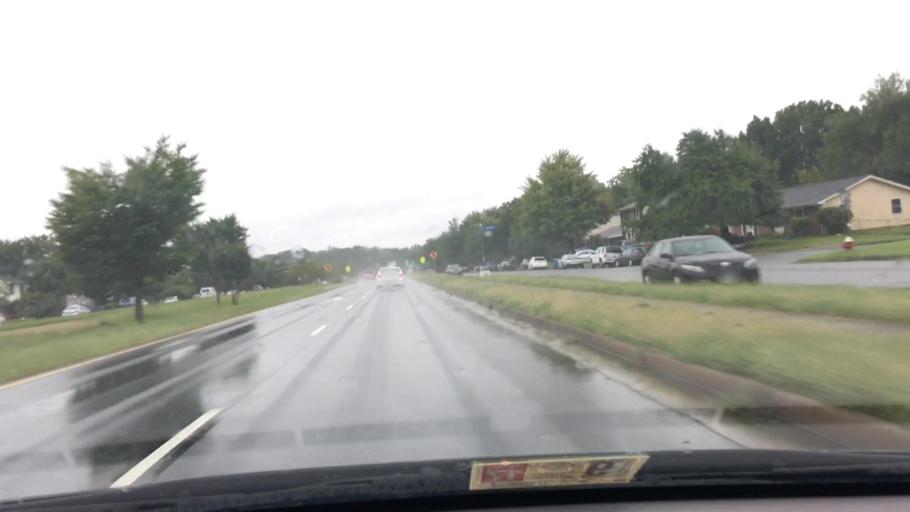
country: US
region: Virginia
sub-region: Loudoun County
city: Sugarland Run
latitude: 39.0138
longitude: -77.3925
